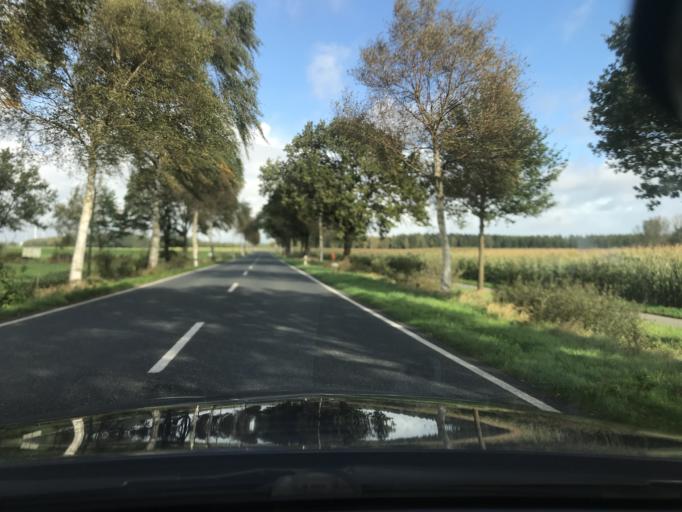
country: DE
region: Lower Saxony
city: Harsefeld
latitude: 53.4795
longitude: 9.4932
